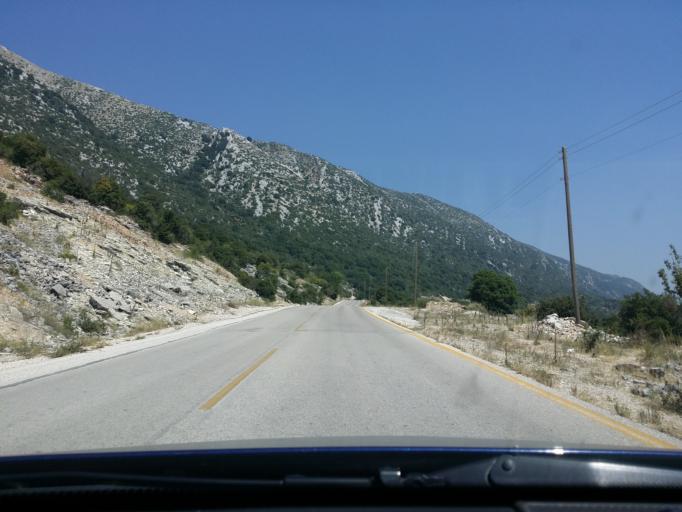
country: GR
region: Epirus
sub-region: Nomos Artas
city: Kampi
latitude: 39.2894
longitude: 20.9756
